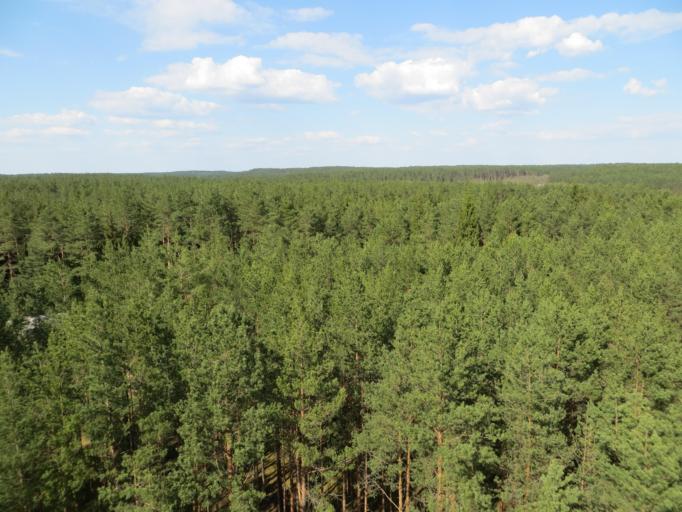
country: LT
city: Svencioneliai
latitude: 55.1728
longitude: 25.9815
